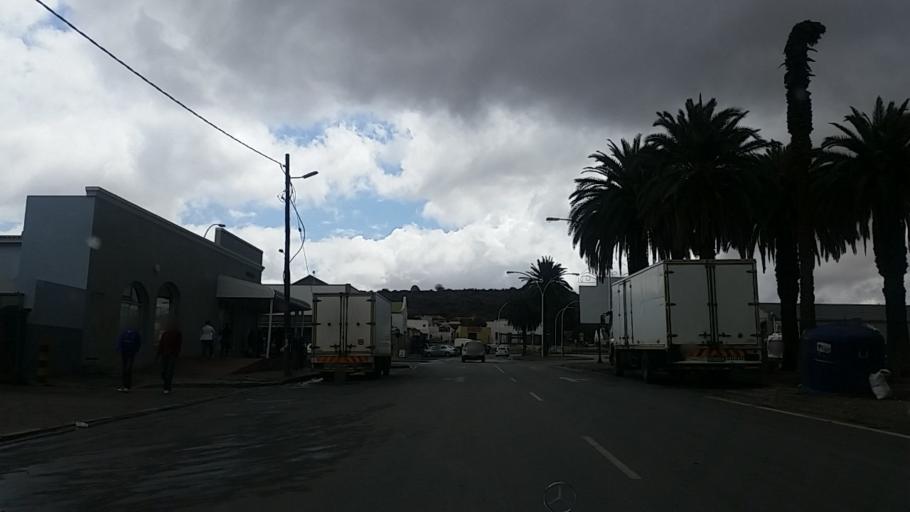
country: ZA
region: Eastern Cape
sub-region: Cacadu District Municipality
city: Graaff-Reinet
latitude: -32.2488
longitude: 24.5377
